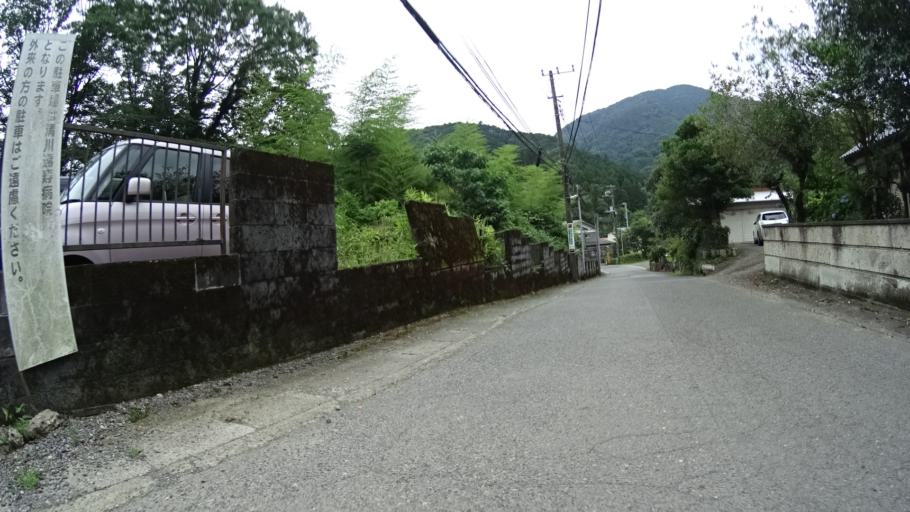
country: JP
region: Kanagawa
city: Atsugi
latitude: 35.4898
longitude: 139.2721
